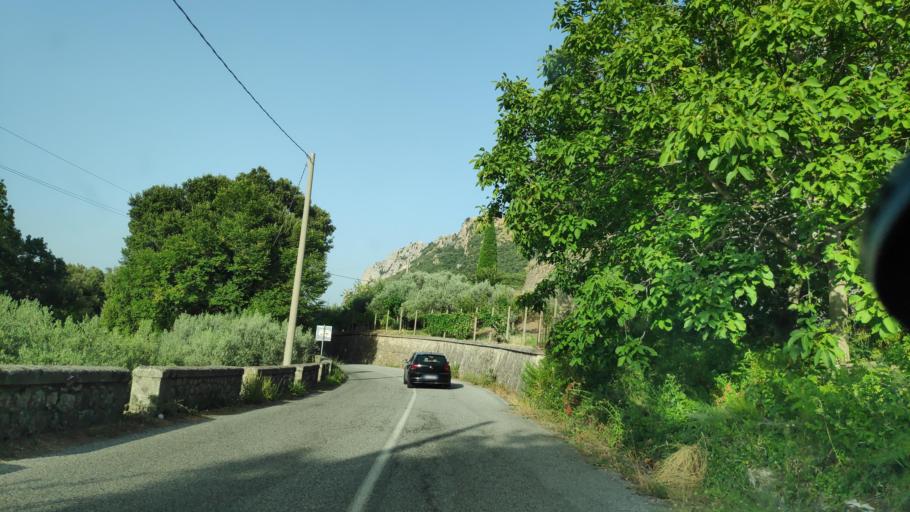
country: IT
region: Calabria
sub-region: Provincia di Reggio Calabria
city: Pazzano
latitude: 38.4788
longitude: 16.4476
